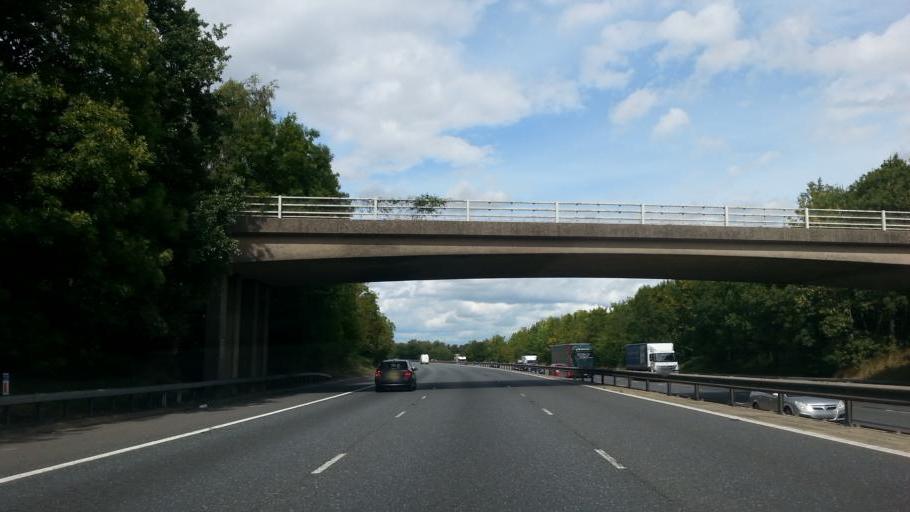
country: GB
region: England
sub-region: Essex
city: Little Hallingbury
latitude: 51.8345
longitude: 0.1933
